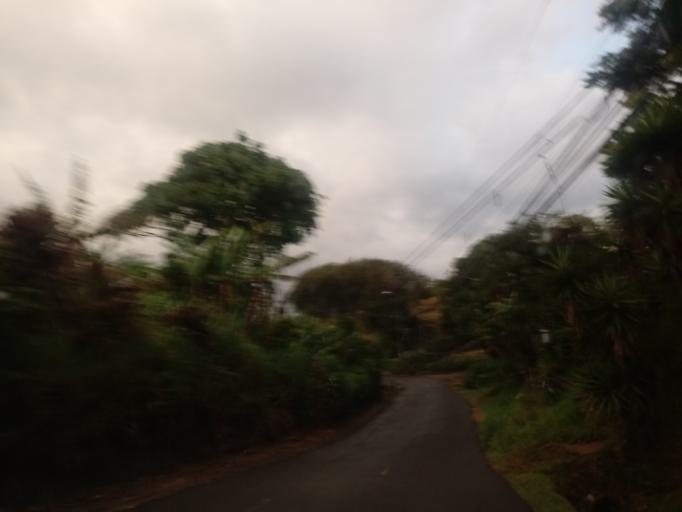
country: CR
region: Heredia
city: Angeles
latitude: 10.0258
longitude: -84.0402
